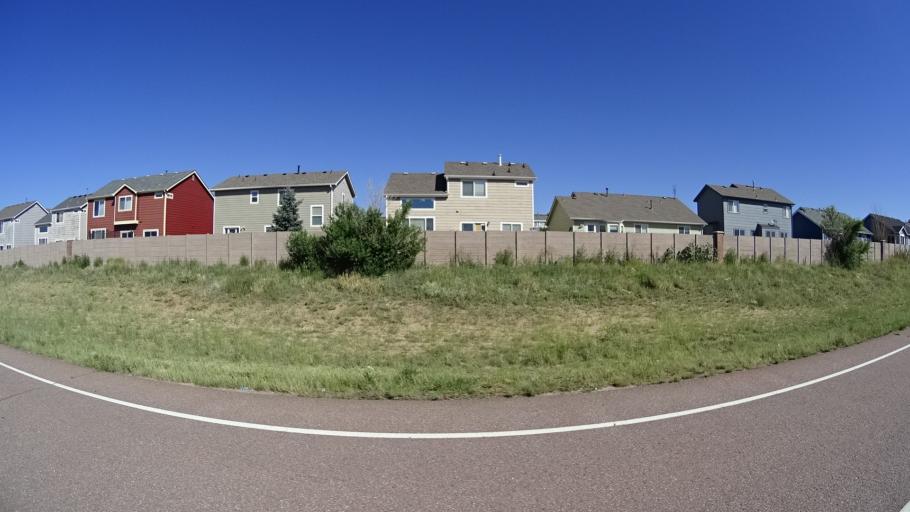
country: US
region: Colorado
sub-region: El Paso County
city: Cimarron Hills
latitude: 38.8594
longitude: -104.6716
